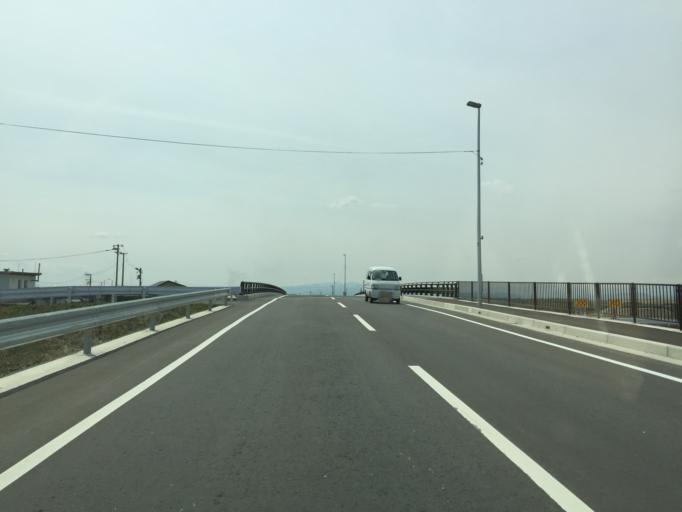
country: JP
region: Yamagata
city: Higashine
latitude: 38.4518
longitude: 140.3580
